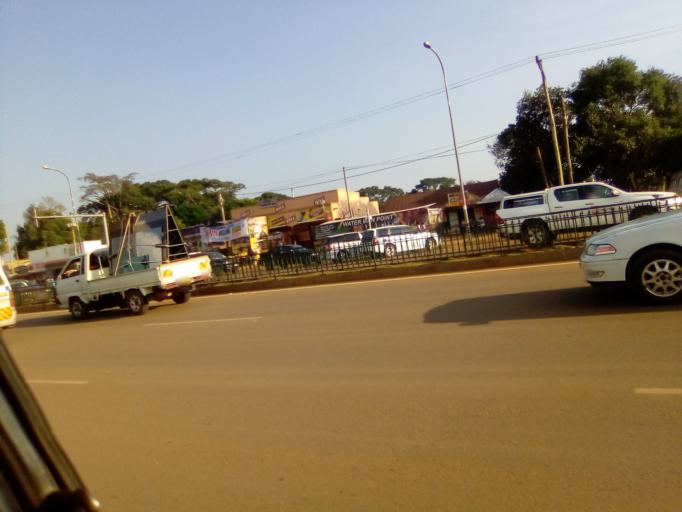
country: UG
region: Central Region
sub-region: Wakiso District
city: Entebbe
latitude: 0.0910
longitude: 32.4946
